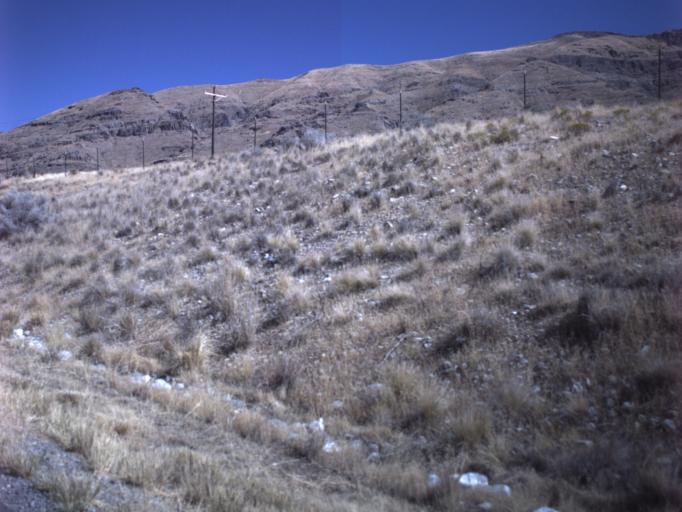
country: US
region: Utah
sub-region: Tooele County
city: Grantsville
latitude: 40.6674
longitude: -112.6753
